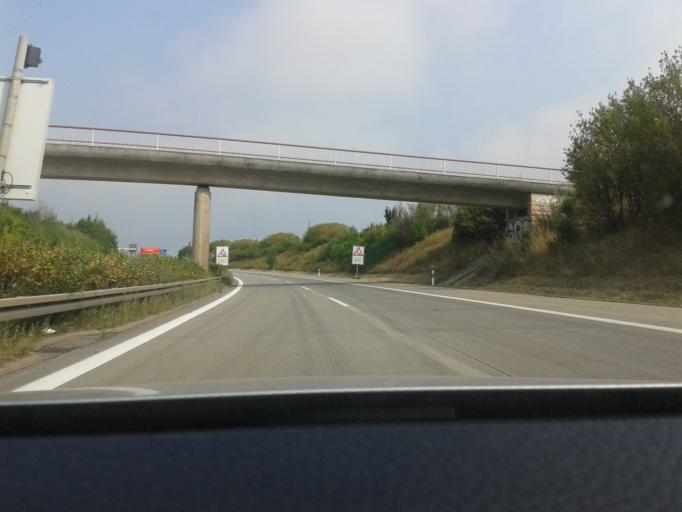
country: DE
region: Saxony
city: Freital
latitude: 51.0471
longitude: 13.6077
